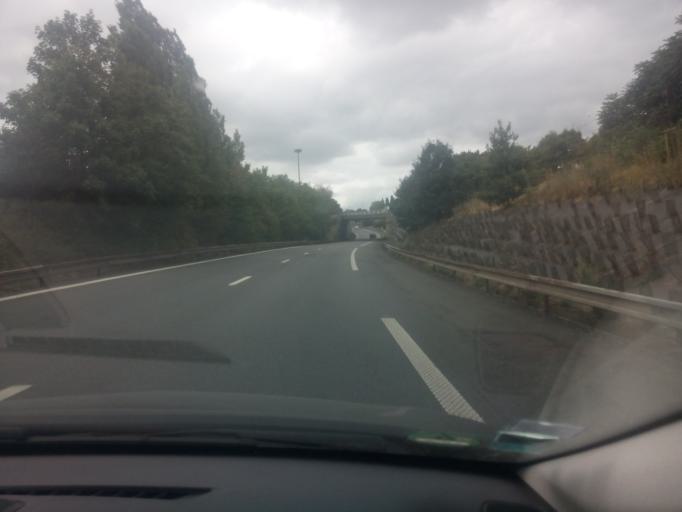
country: FR
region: Ile-de-France
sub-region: Departement de l'Essonne
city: Wissous
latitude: 48.7408
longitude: 2.3198
